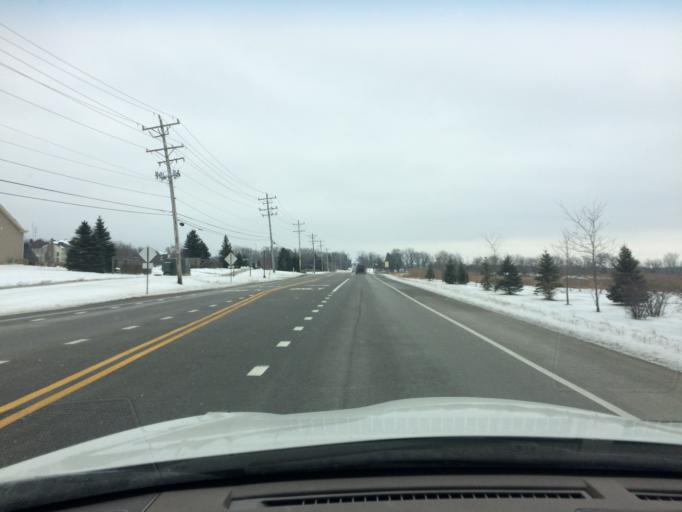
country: US
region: Illinois
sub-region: Kane County
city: Saint Charles
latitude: 41.8968
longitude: -88.3596
